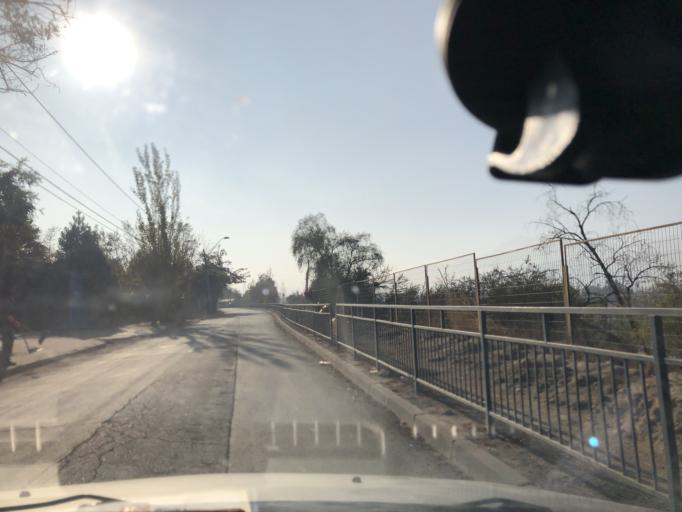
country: CL
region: Santiago Metropolitan
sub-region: Provincia de Cordillera
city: Puente Alto
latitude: -33.6282
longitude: -70.5828
